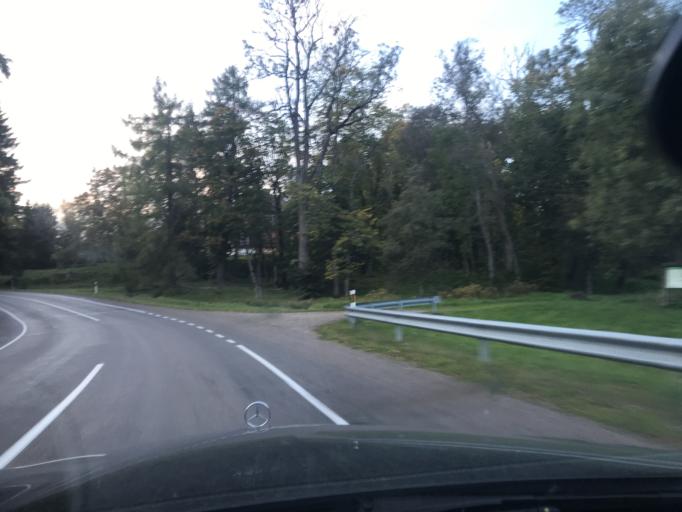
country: EE
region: Valgamaa
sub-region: Torva linn
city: Torva
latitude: 58.0085
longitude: 26.2068
